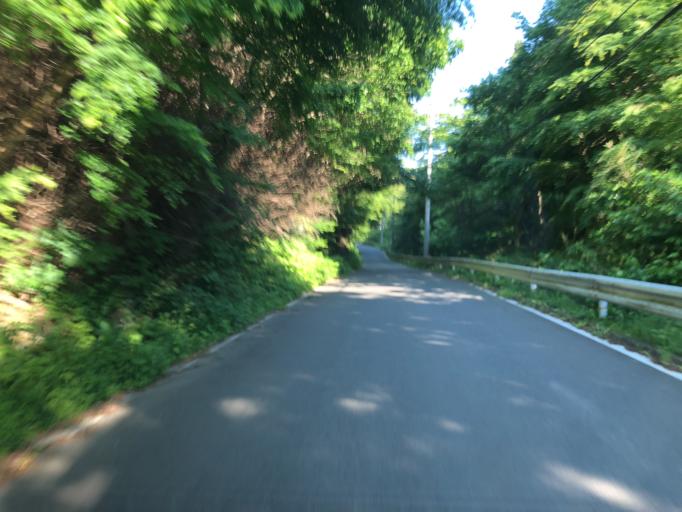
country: JP
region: Ibaraki
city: Kitaibaraki
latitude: 36.8684
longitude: 140.6581
